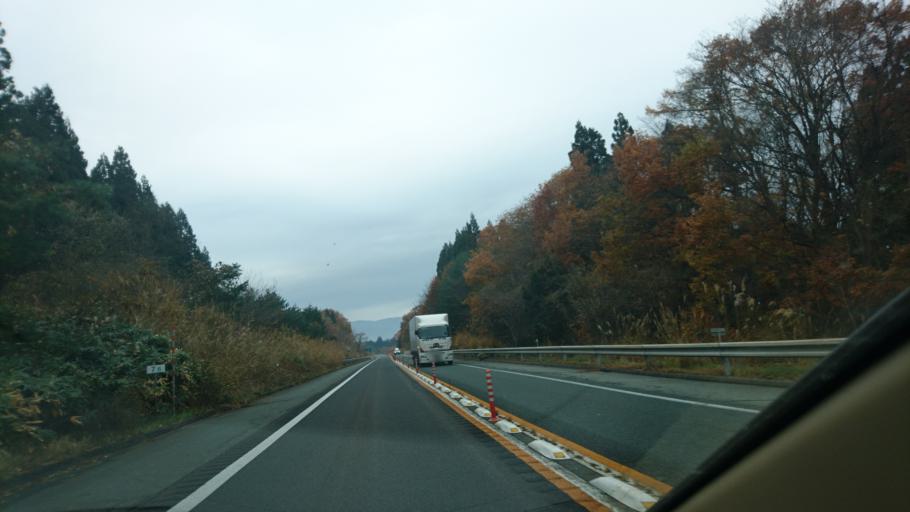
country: JP
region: Iwate
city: Kitakami
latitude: 39.2860
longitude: 140.9948
